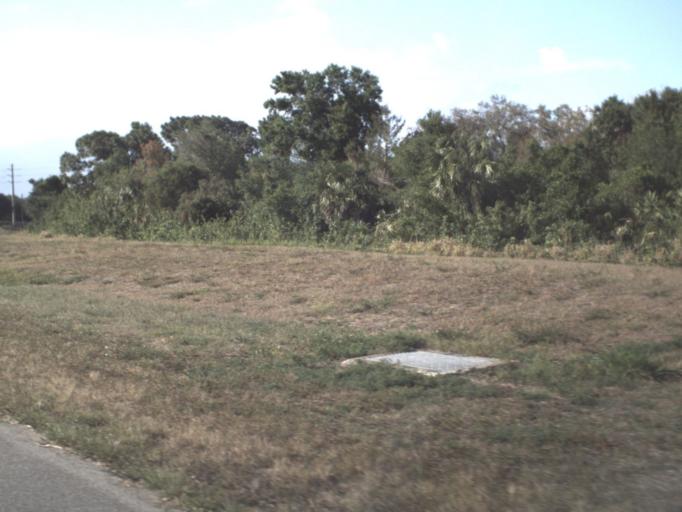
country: US
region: Florida
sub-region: Brevard County
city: Melbourne
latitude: 28.1115
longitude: -80.6333
